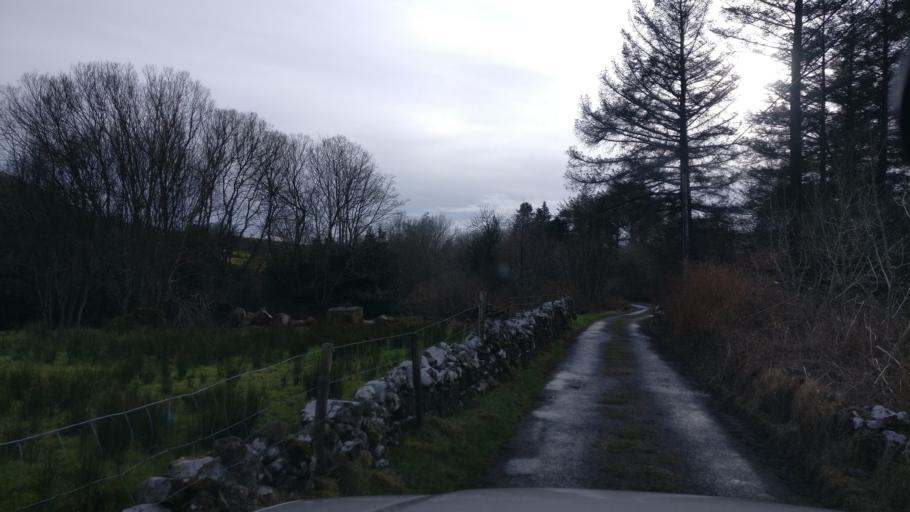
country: IE
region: Connaught
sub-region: County Galway
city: Oughterard
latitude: 53.5556
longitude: -9.4424
